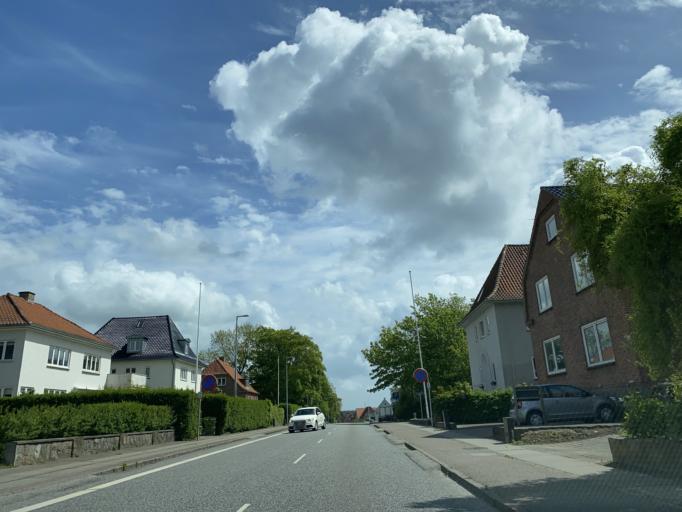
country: DK
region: South Denmark
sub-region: Sonderborg Kommune
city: Sonderborg
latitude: 54.9067
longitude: 9.7972
